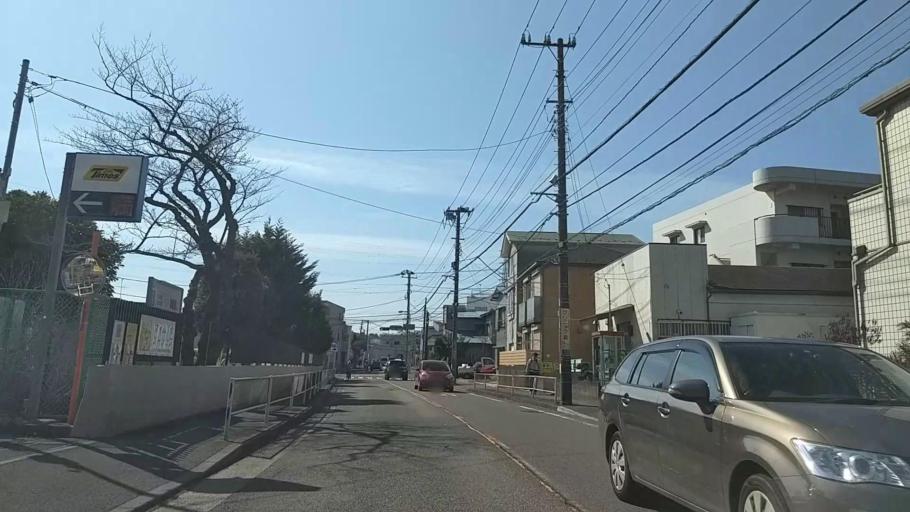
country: JP
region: Kanagawa
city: Kamakura
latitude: 35.3493
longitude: 139.5358
